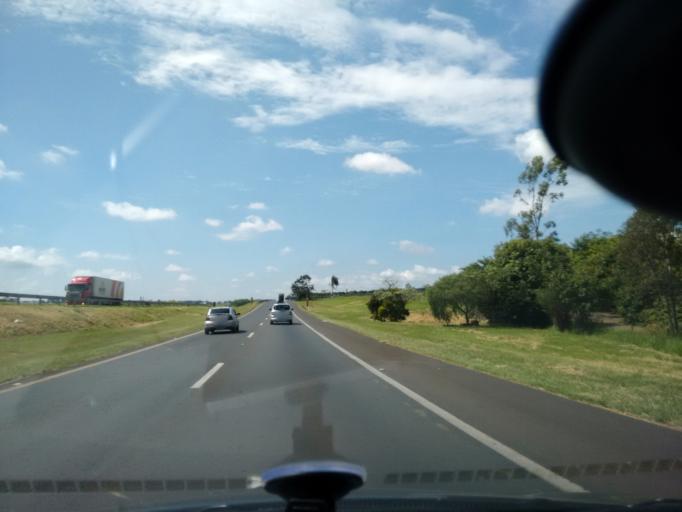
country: BR
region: Sao Paulo
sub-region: Sao Carlos
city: Sao Carlos
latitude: -21.9799
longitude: -47.9217
